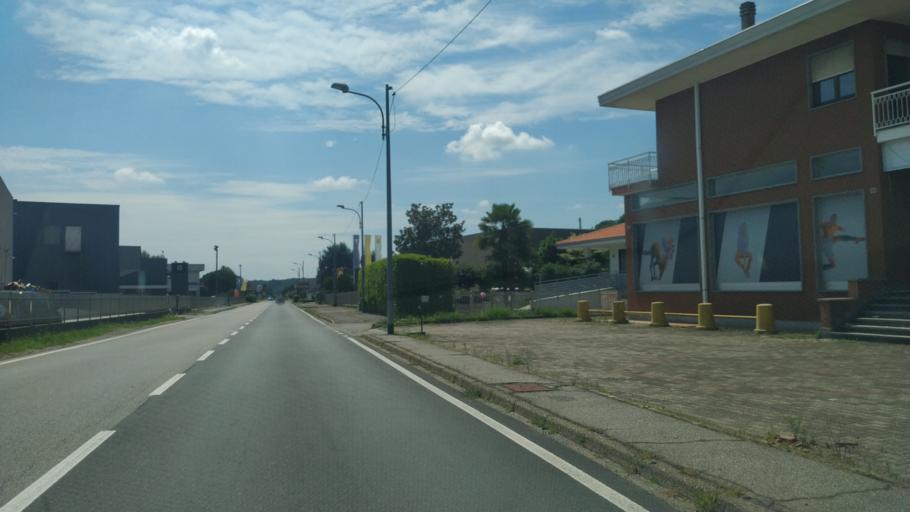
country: IT
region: Piedmont
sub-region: Provincia di Novara
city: Cureggio
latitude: 45.6857
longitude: 8.4566
